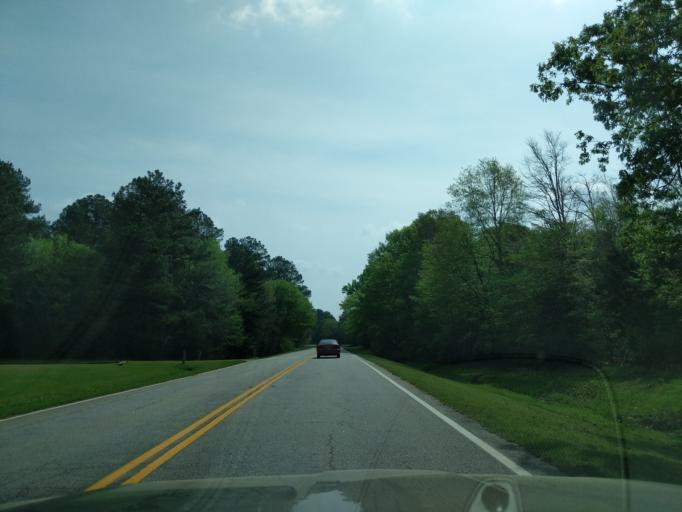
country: US
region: Georgia
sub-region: Lincoln County
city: Lincolnton
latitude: 33.8056
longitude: -82.4038
